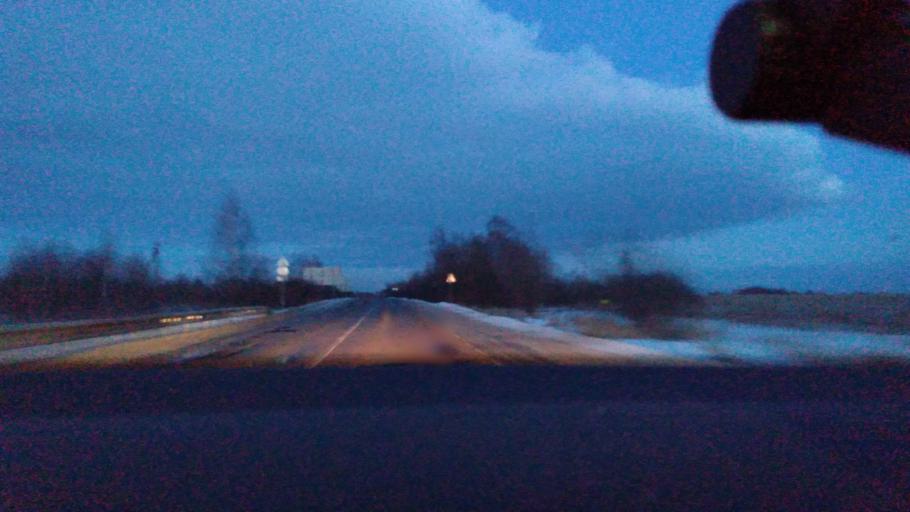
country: RU
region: Moskovskaya
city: Krasnaya Poyma
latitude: 55.1674
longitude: 39.1603
